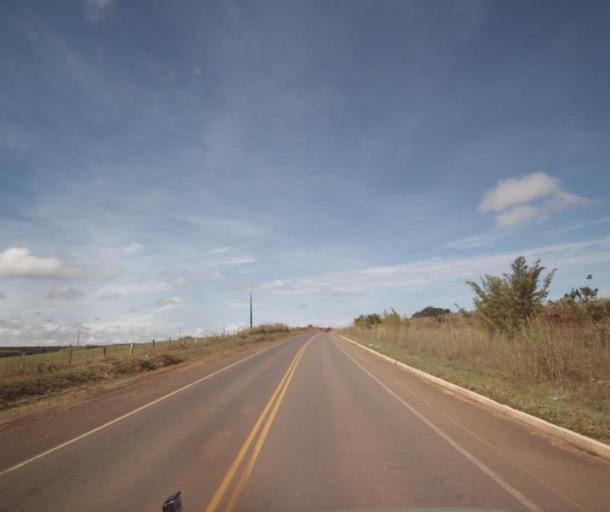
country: BR
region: Goias
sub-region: Anapolis
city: Anapolis
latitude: -16.1801
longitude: -48.9019
